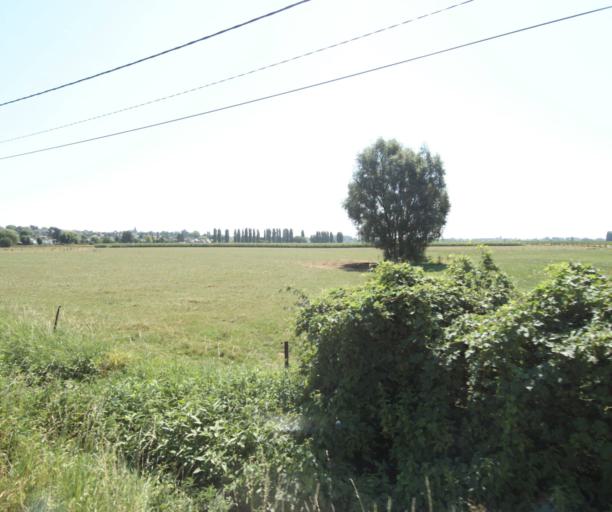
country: FR
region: Nord-Pas-de-Calais
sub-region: Departement du Nord
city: Roncq
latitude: 50.7563
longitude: 3.1049
